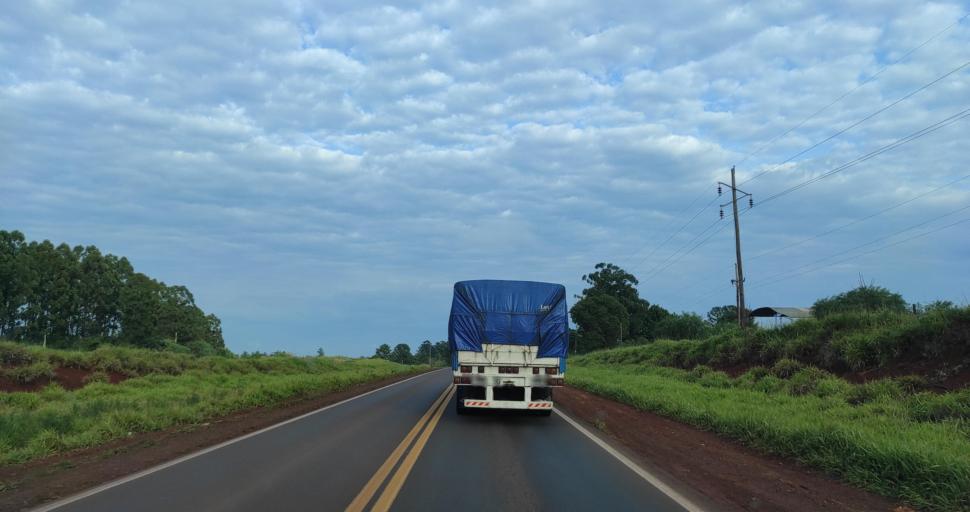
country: AR
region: Corrientes
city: Gobernador Ingeniero Valentin Virasoro
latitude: -27.9392
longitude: -55.9791
